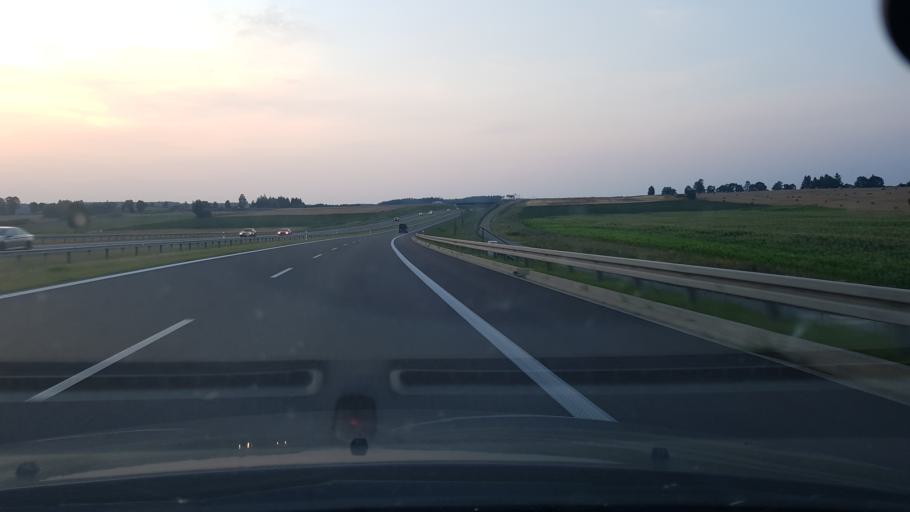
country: PL
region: Warmian-Masurian Voivodeship
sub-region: Powiat nidzicki
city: Nidzica
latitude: 53.3490
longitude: 20.3933
